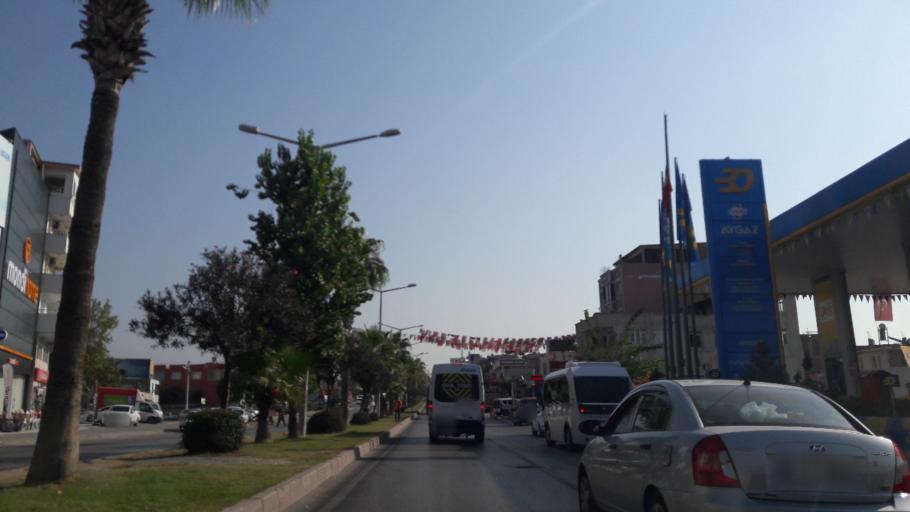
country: TR
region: Adana
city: Yuregir
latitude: 37.0343
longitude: 35.4151
